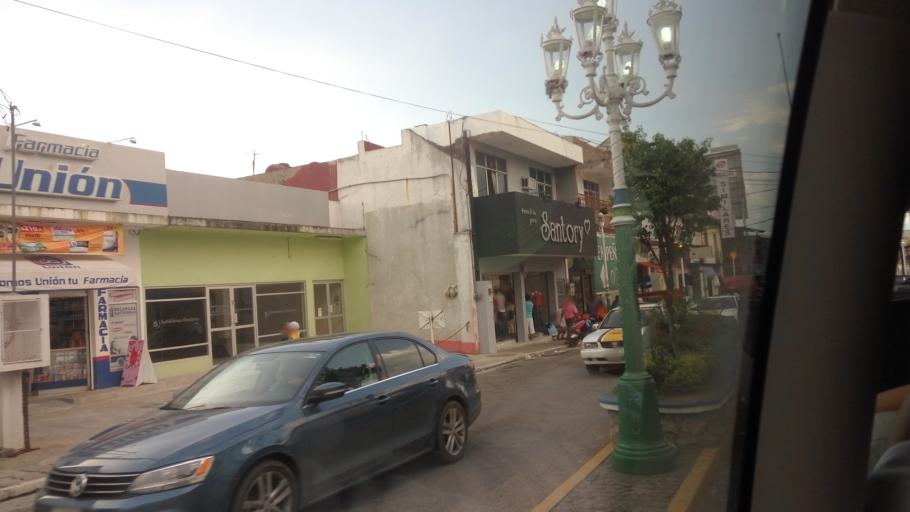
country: MX
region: Tabasco
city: Teapa
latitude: 17.5496
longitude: -92.9528
